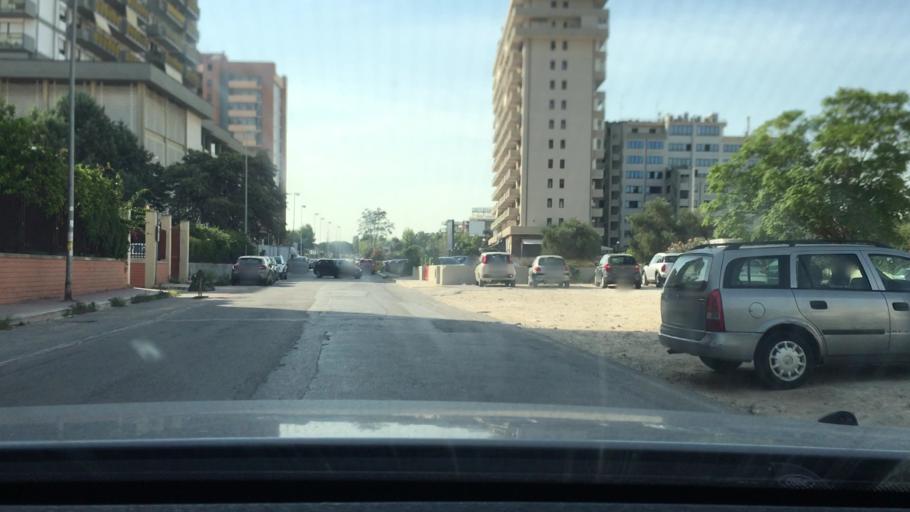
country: IT
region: Apulia
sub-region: Provincia di Bari
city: Bari
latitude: 41.1018
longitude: 16.8845
